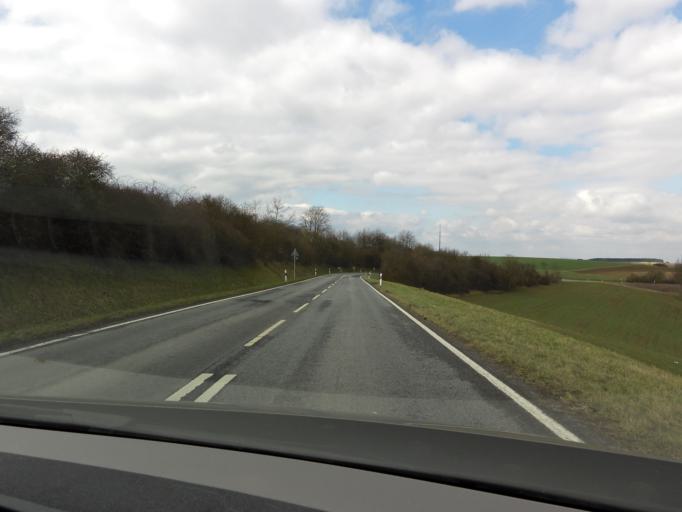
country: DE
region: Bavaria
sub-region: Regierungsbezirk Unterfranken
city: Arnstein
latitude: 49.9630
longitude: 9.9802
